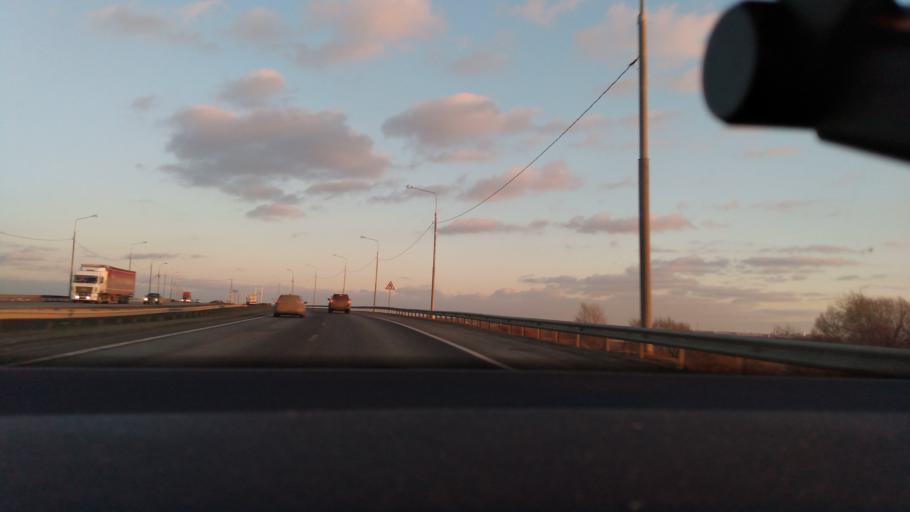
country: RU
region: Moskovskaya
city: Raduzhnyy
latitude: 55.1426
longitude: 38.7387
